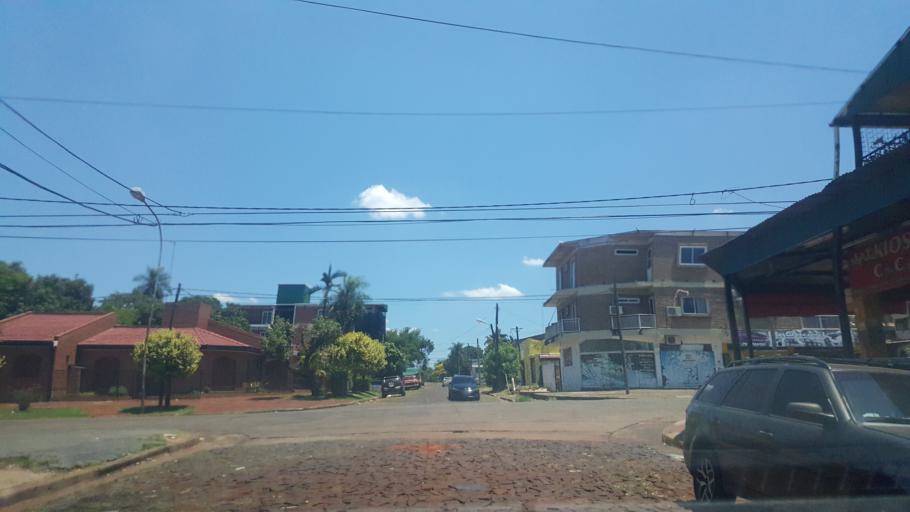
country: AR
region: Misiones
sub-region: Departamento de Capital
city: Posadas
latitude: -27.3867
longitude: -55.9051
